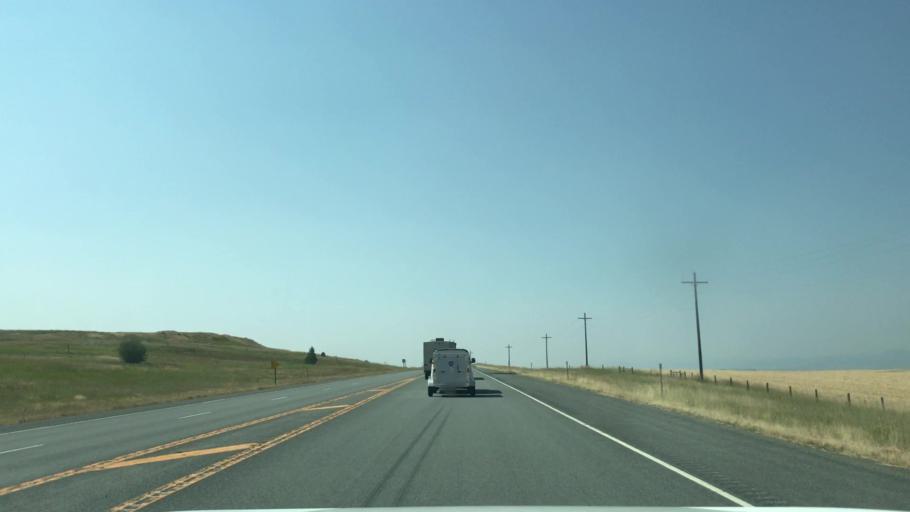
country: US
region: Montana
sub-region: Lewis and Clark County
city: East Helena
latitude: 46.5471
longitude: -111.7499
